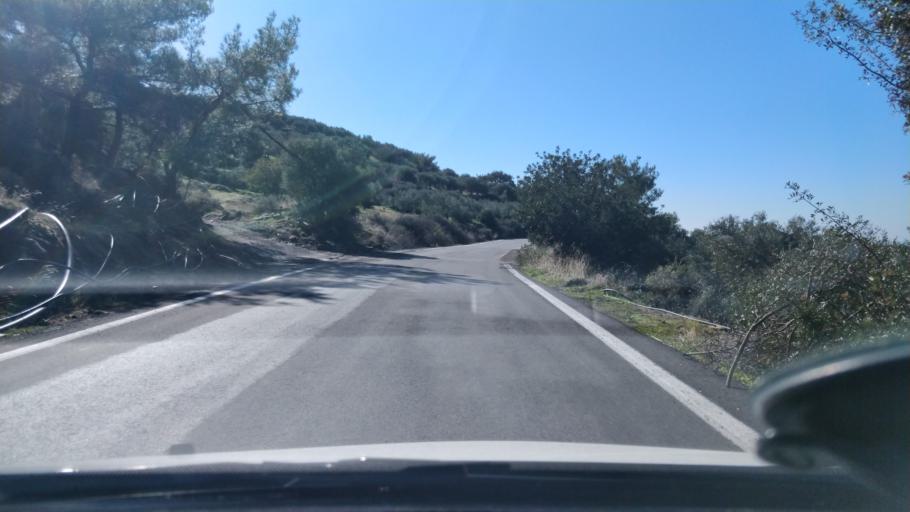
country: GR
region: Crete
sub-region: Nomos Irakleiou
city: Kastelli
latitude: 35.0175
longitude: 25.4490
